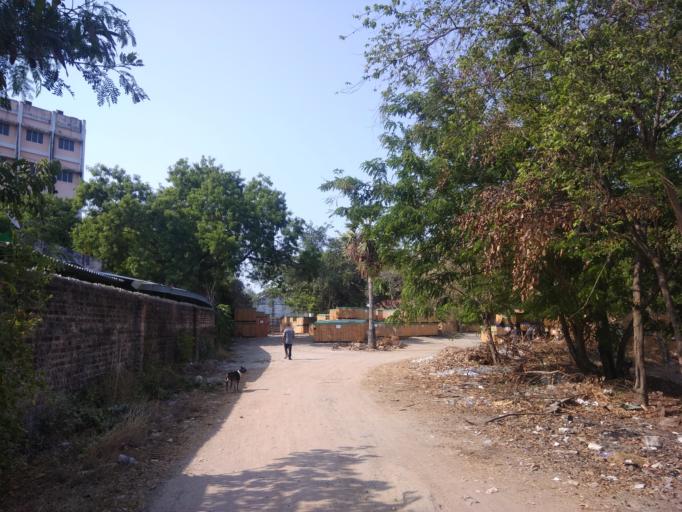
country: IN
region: Tamil Nadu
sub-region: Kancheepuram
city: Alandur
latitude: 13.0090
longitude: 80.2185
